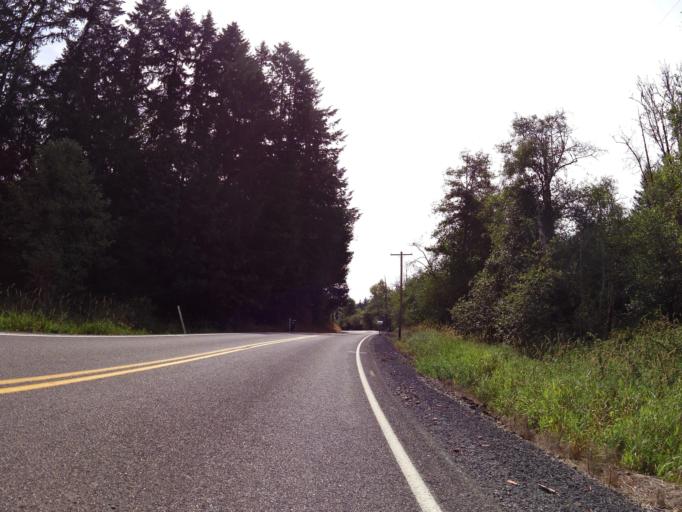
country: US
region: Washington
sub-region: Lewis County
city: Napavine
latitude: 46.5704
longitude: -122.9682
